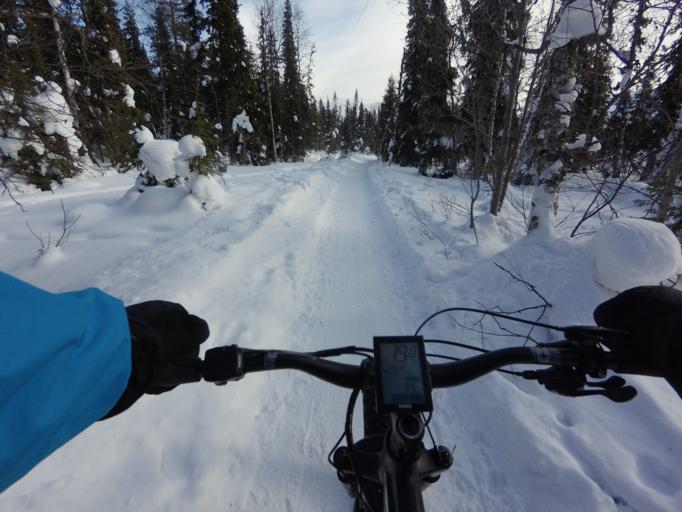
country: FI
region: Lapland
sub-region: Tunturi-Lappi
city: Kolari
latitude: 67.6034
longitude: 24.2235
